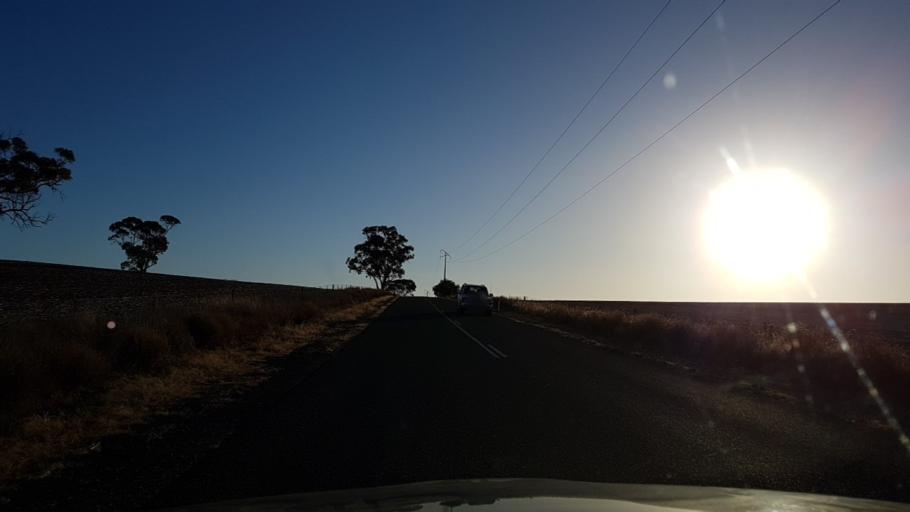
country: AU
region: South Australia
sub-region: Clare and Gilbert Valleys
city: Clare
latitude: -34.0186
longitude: 138.7118
